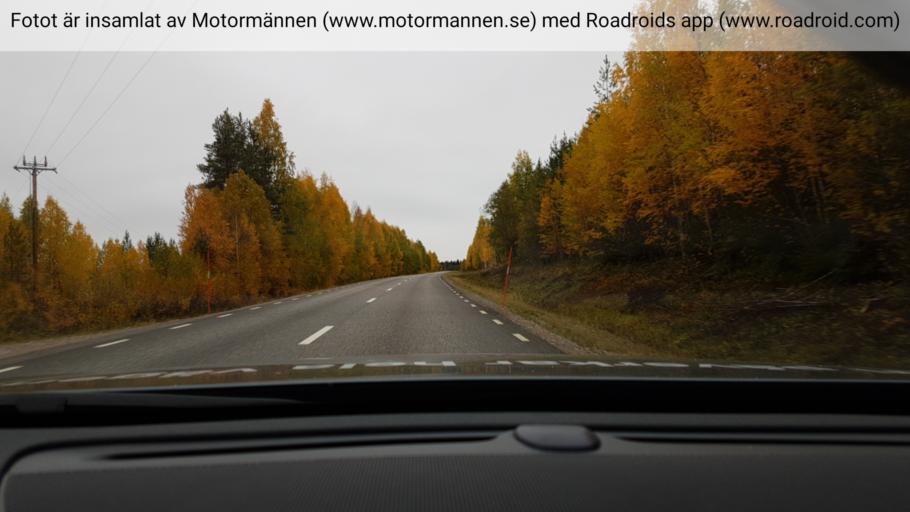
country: SE
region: Norrbotten
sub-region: Overkalix Kommun
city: OEverkalix
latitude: 66.5456
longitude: 22.7548
